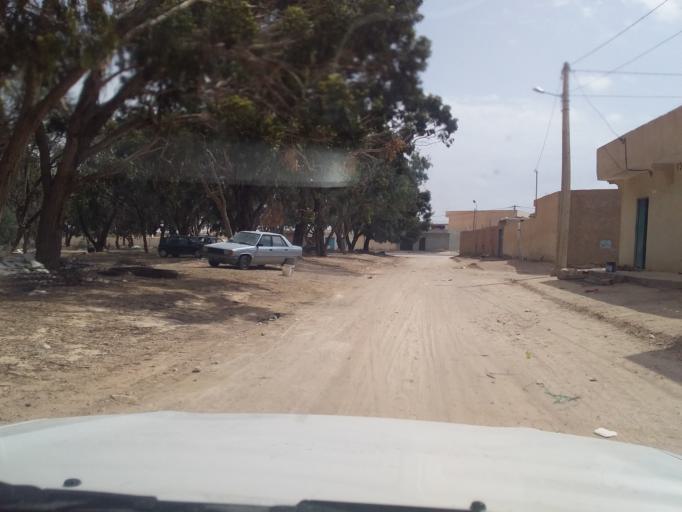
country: TN
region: Qabis
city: Matmata
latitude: 33.6206
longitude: 10.2758
